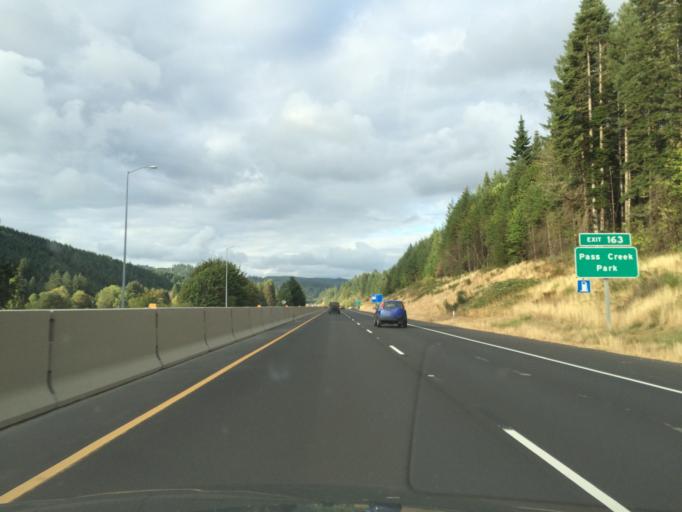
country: US
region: Oregon
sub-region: Douglas County
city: Drain
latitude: 43.7182
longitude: -123.2120
